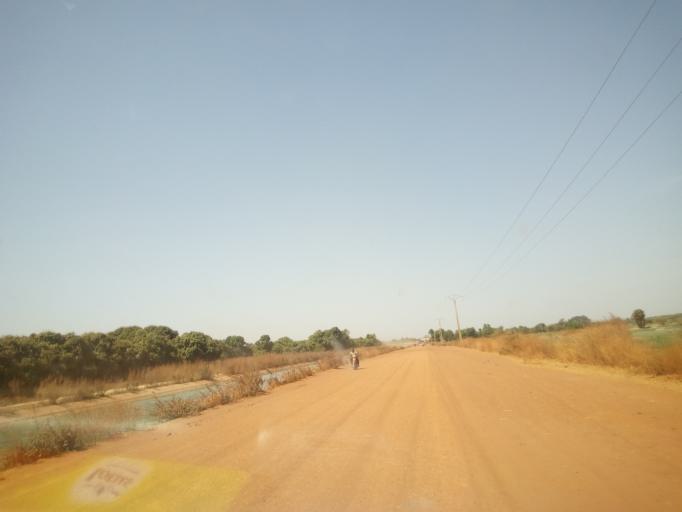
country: ML
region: Bamako
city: Bamako
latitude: 12.6209
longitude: -7.7662
